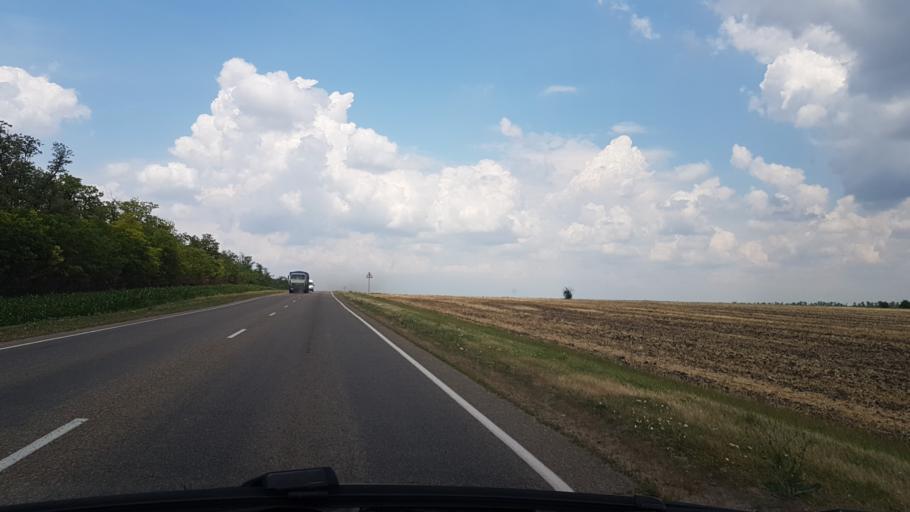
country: RU
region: Krasnodarskiy
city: Dmitriyevskaya
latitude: 45.6771
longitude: 40.7440
